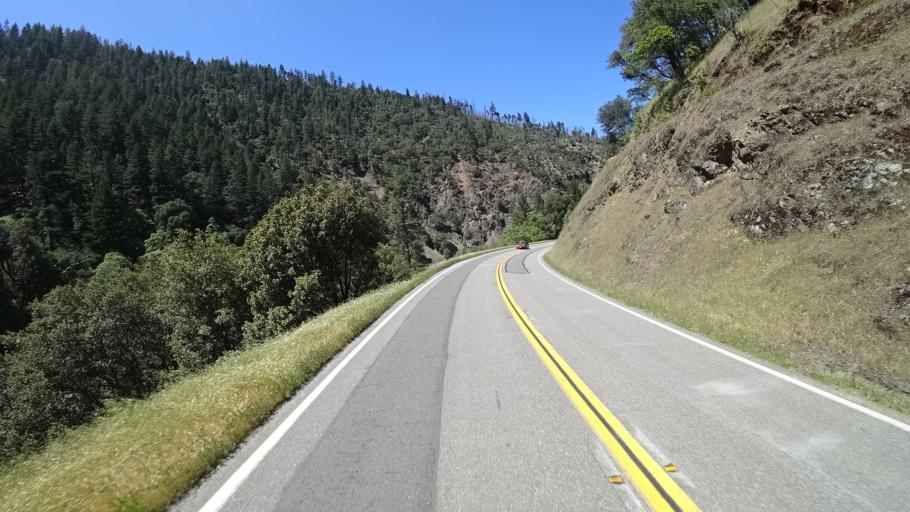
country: US
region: California
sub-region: Trinity County
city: Hayfork
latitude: 40.7533
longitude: -123.2832
